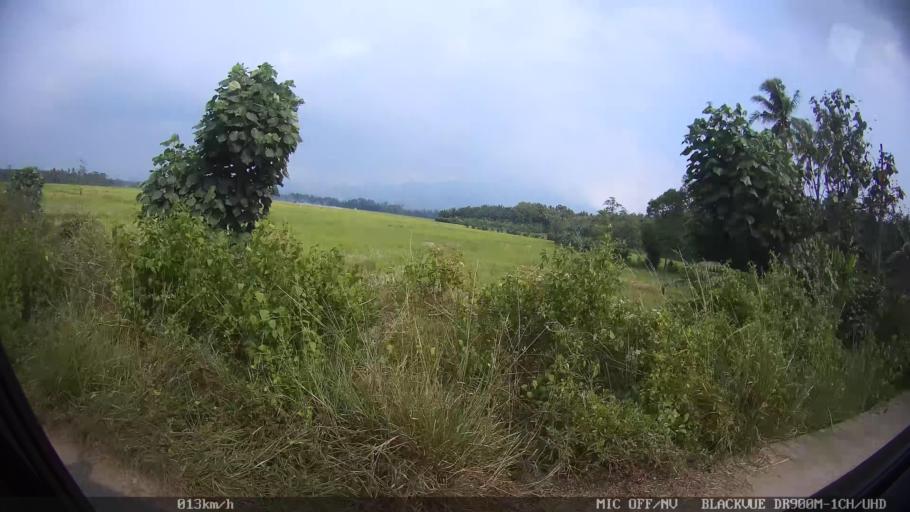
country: ID
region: Lampung
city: Kedondong
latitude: -5.4088
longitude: 105.0164
